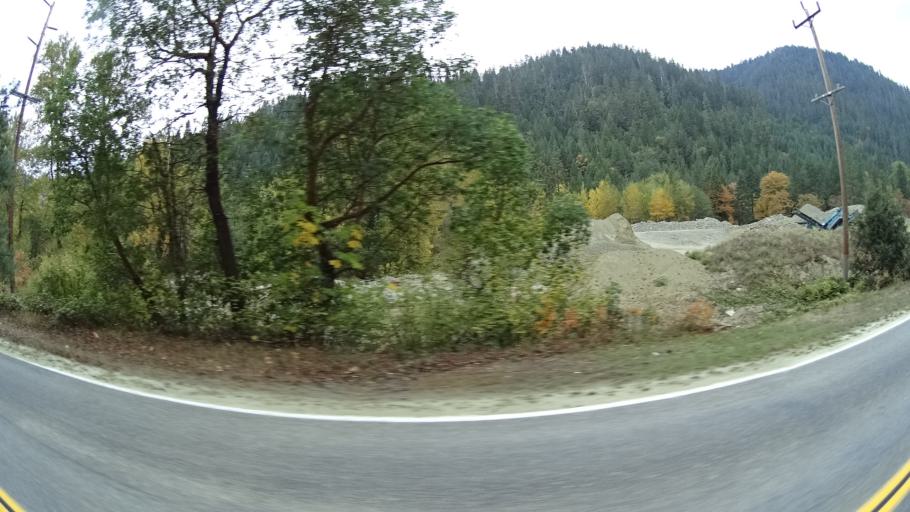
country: US
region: California
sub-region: Siskiyou County
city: Happy Camp
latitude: 41.8846
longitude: -123.4317
